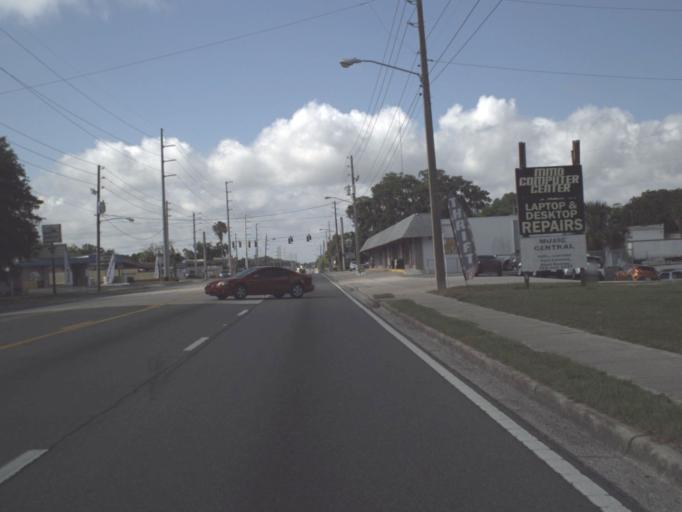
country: US
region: Florida
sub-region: Lake County
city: Leesburg
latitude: 28.8070
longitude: -81.8877
